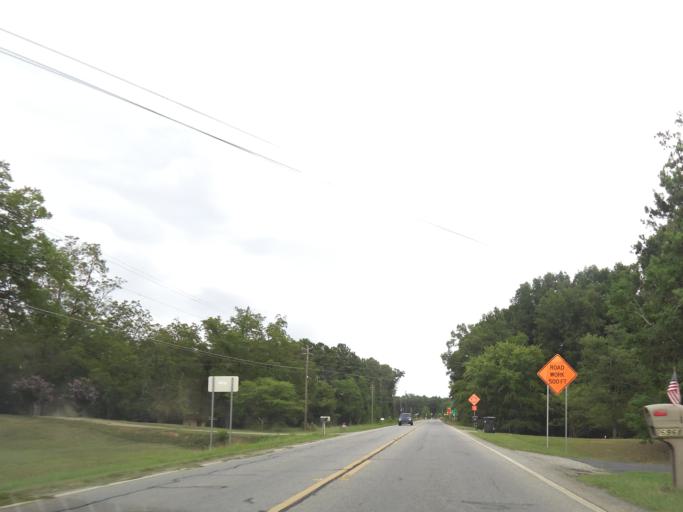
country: US
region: Georgia
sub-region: Bibb County
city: West Point
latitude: 32.8538
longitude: -83.7889
